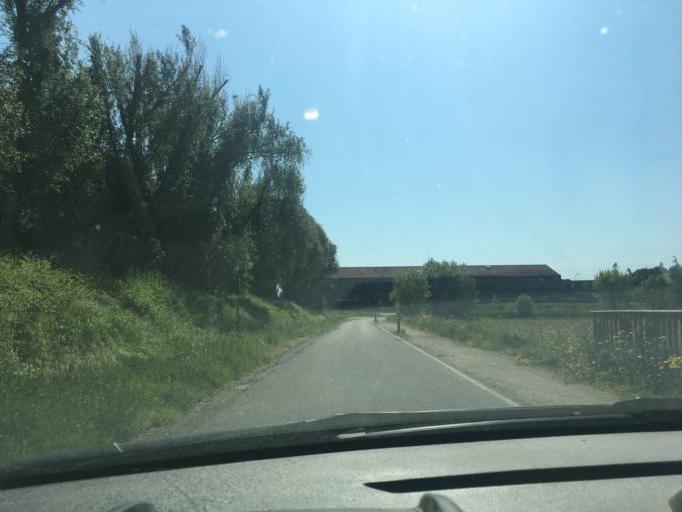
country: FR
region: Poitou-Charentes
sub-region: Departement de la Charente
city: Cognac
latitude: 45.6839
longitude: -0.3432
